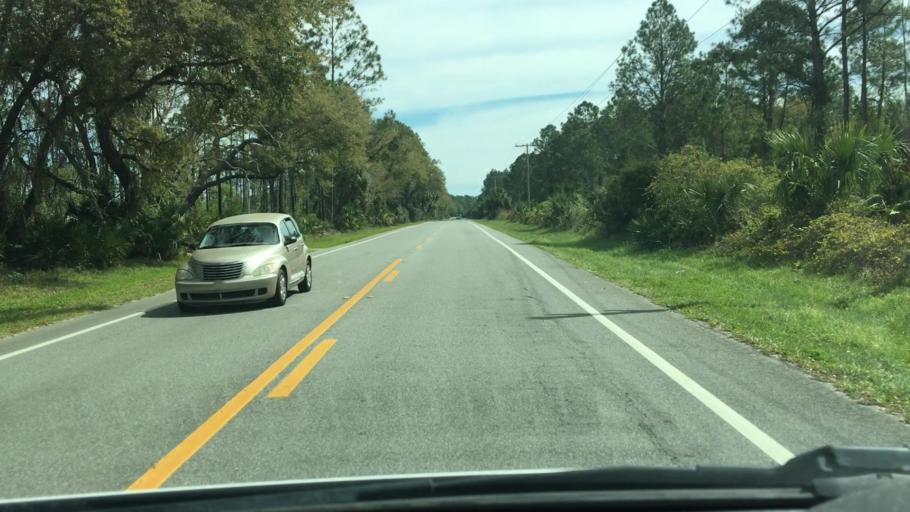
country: US
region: Florida
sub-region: Lake County
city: Lake Mack-Forest Hills
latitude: 29.0091
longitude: -81.4047
